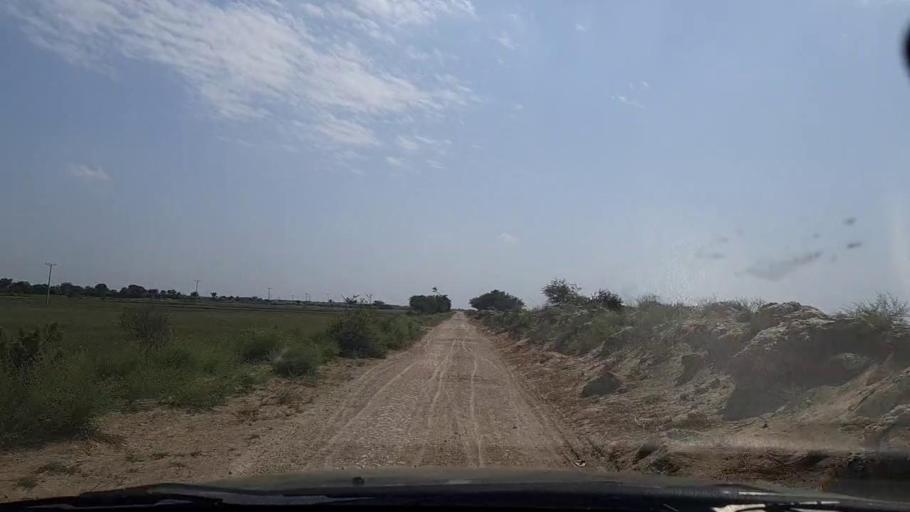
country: PK
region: Sindh
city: Mirpur Batoro
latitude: 24.5848
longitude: 68.1965
